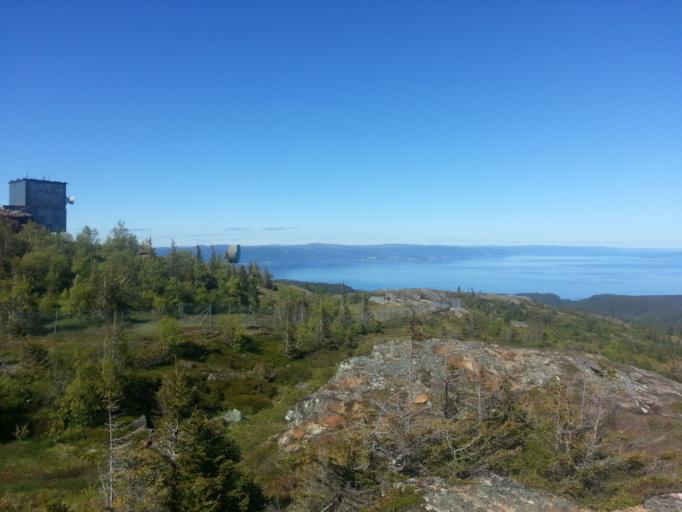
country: NO
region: Sor-Trondelag
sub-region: Melhus
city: Melhus
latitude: 63.4204
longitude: 10.2536
